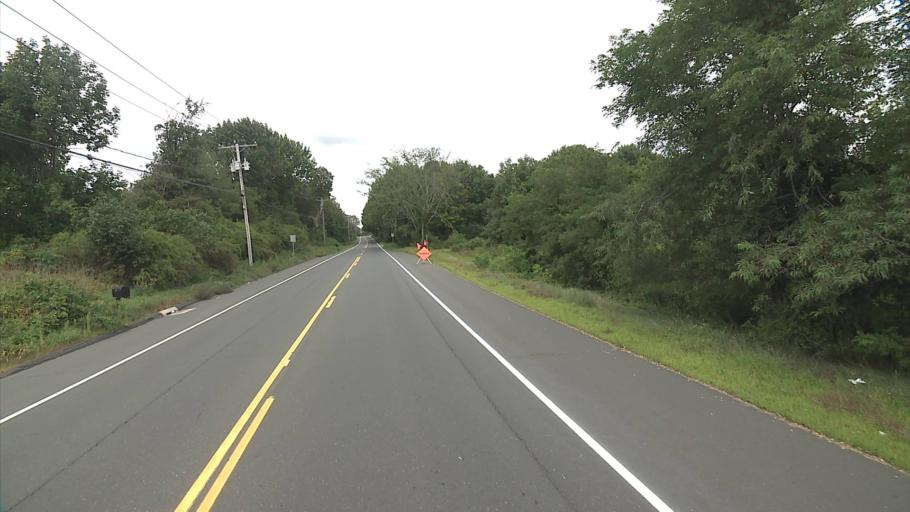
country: US
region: Connecticut
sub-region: New London County
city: Colchester
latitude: 41.5286
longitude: -72.2975
